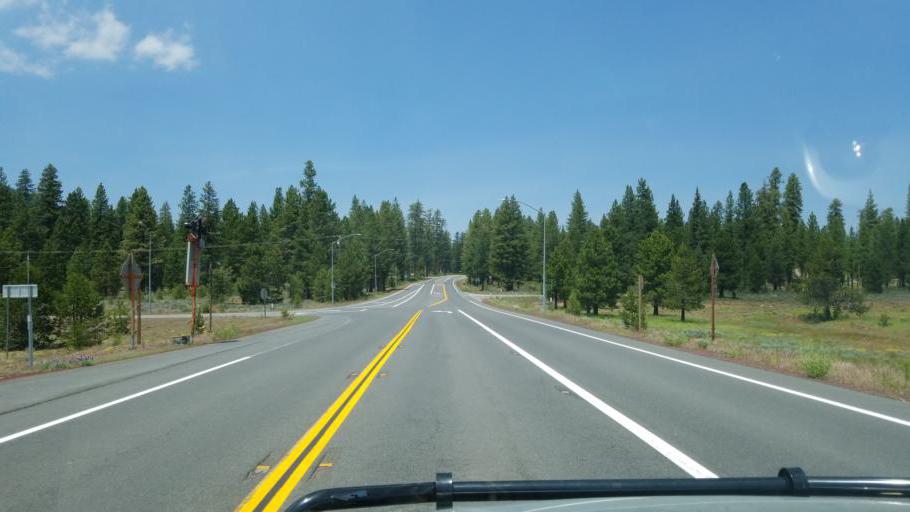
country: US
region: California
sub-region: Lassen County
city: Westwood
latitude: 40.5852
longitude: -121.0876
